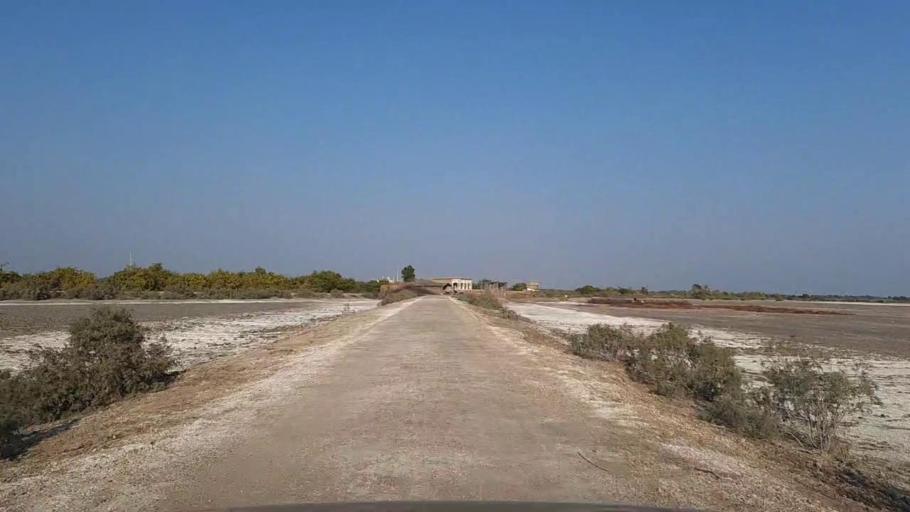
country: PK
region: Sindh
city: Tando Mittha Khan
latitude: 25.9180
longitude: 69.0855
